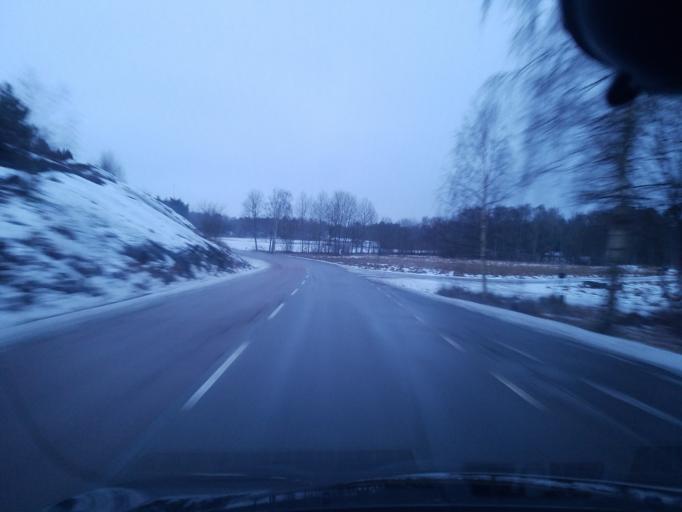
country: SE
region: Vaestra Goetaland
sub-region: Lysekils Kommun
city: Lysekil
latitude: 58.2897
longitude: 11.4768
